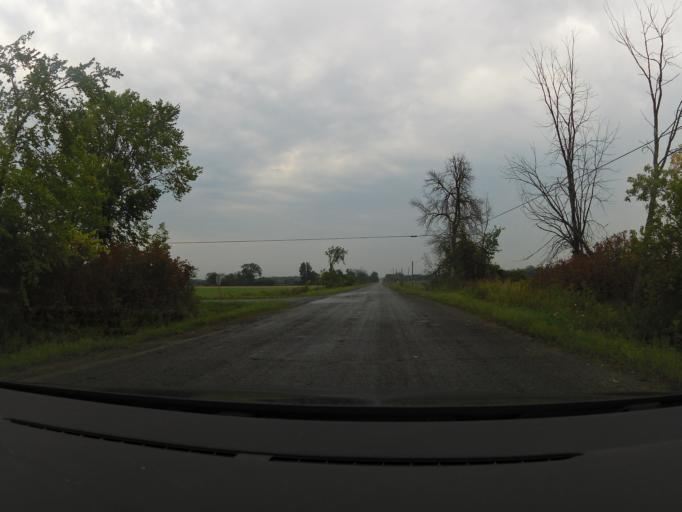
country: CA
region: Ontario
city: Carleton Place
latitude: 45.1825
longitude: -76.0899
